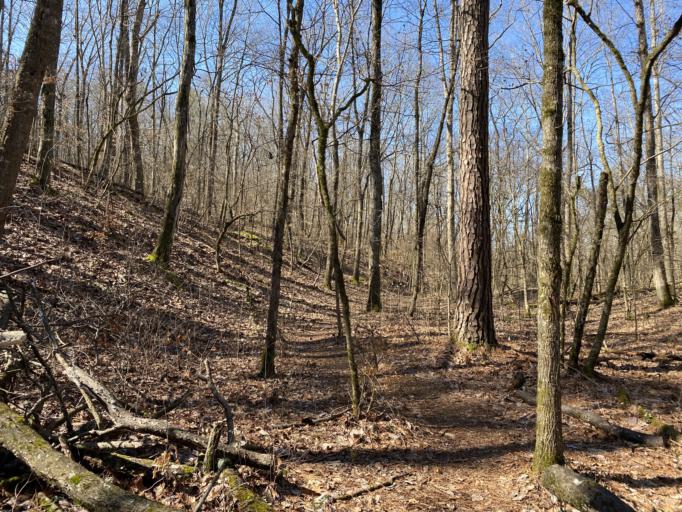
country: US
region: Georgia
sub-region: Gordon County
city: Calhoun
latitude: 34.4653
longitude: -84.9859
